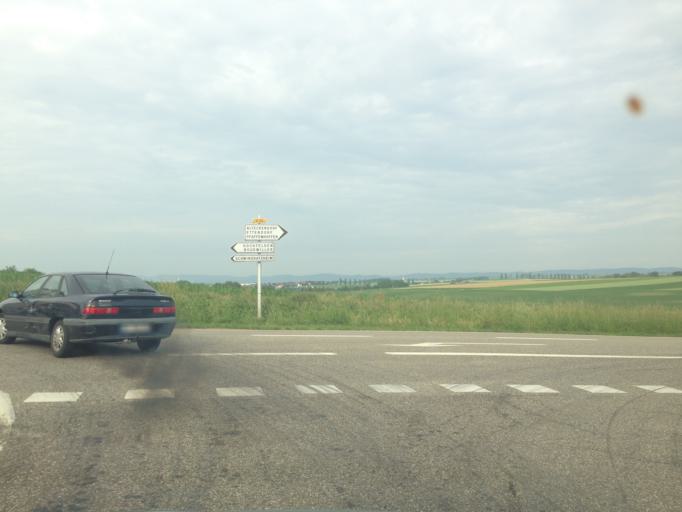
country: FR
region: Alsace
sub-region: Departement du Bas-Rhin
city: Schwindratzheim
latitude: 48.7708
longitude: 7.5966
